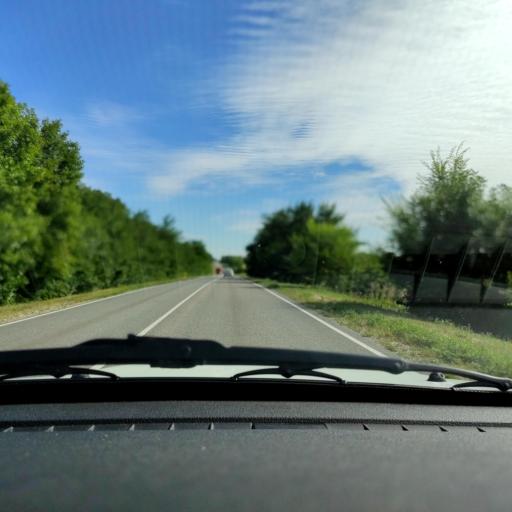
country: RU
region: Voronezj
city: Volya
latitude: 51.7151
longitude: 39.5358
